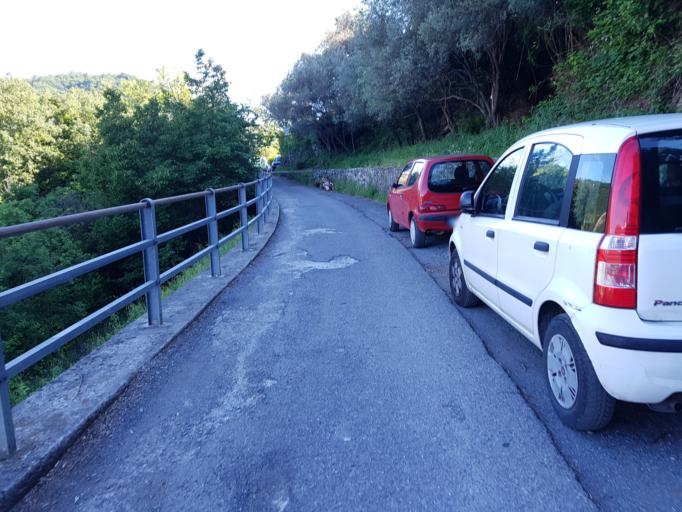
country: IT
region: Liguria
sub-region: Provincia di Genova
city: Piccarello
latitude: 44.4527
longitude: 8.9731
